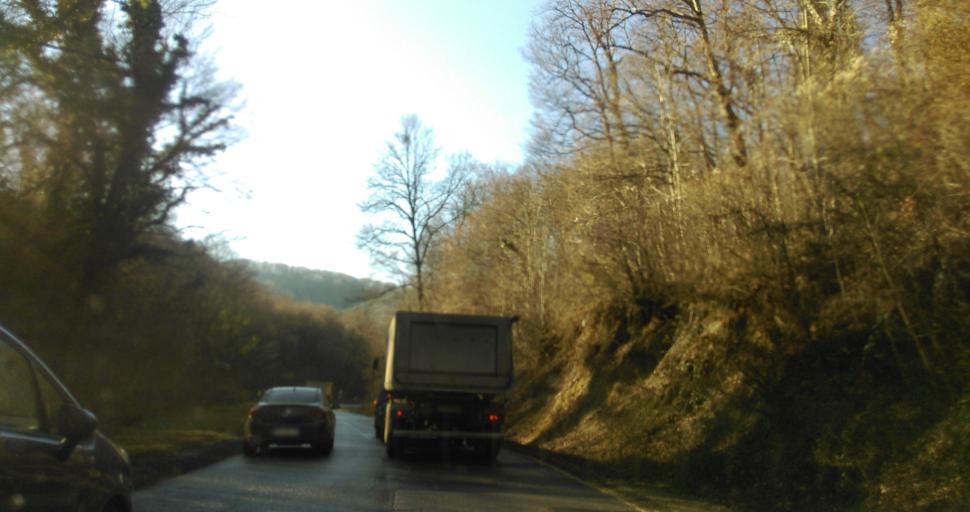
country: RS
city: Vrdnik
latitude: 45.1745
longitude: 19.8317
